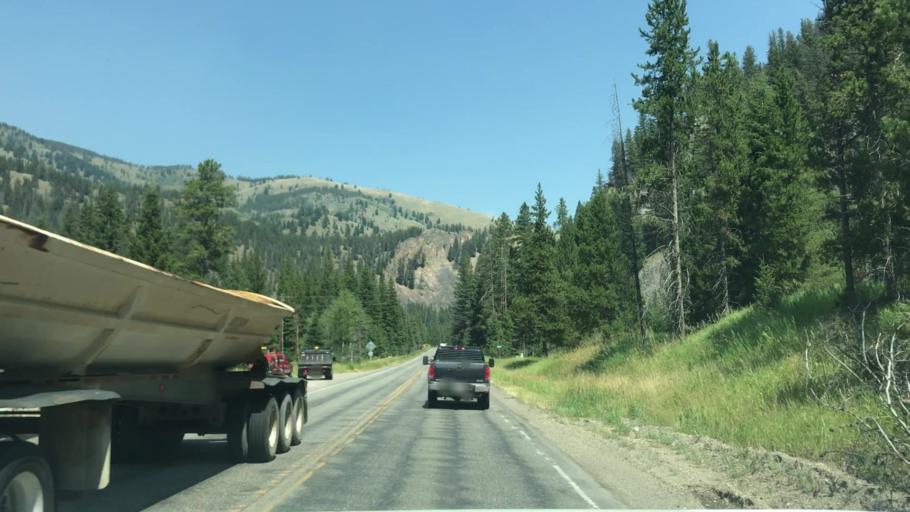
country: US
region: Montana
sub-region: Gallatin County
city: Big Sky
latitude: 45.2901
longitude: -111.2174
